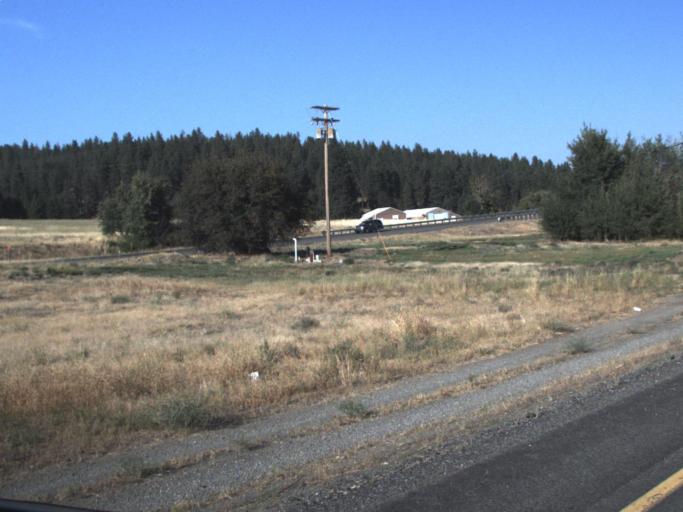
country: US
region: Washington
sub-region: Spokane County
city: Liberty Lake
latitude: 47.7004
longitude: -117.1520
